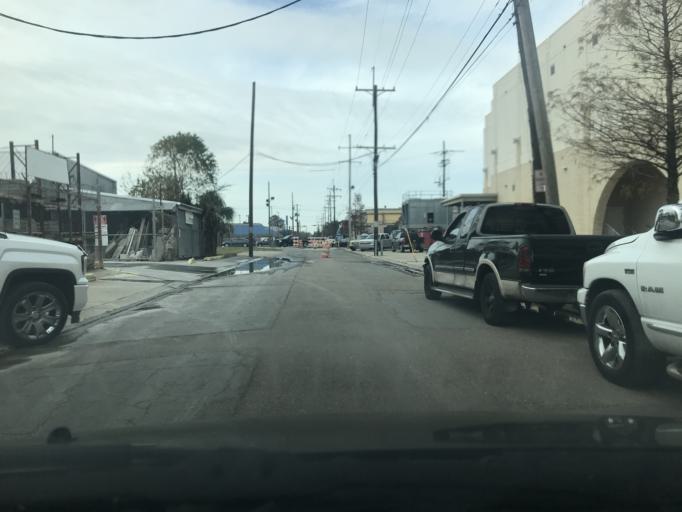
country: US
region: Louisiana
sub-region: Orleans Parish
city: New Orleans
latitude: 29.9633
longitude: -90.1098
